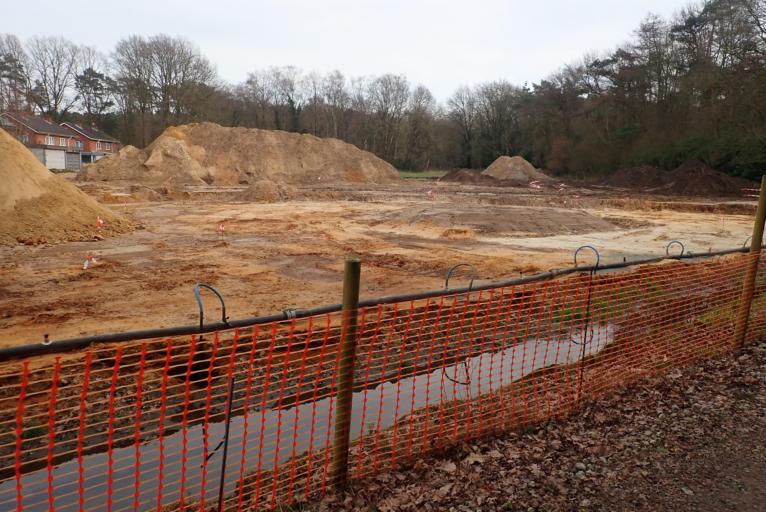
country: BE
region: Flanders
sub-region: Provincie Oost-Vlaanderen
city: Sint-Niklaas
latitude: 51.1785
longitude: 4.1953
